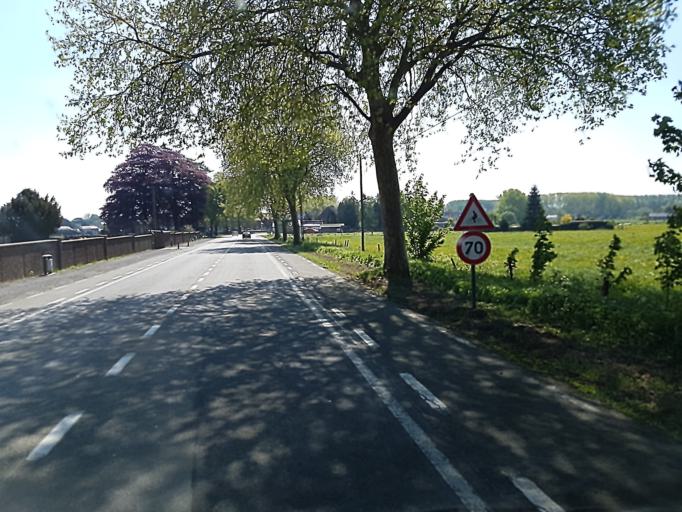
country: BE
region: Wallonia
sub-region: Province du Hainaut
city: Lens
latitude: 50.5624
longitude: 3.8923
